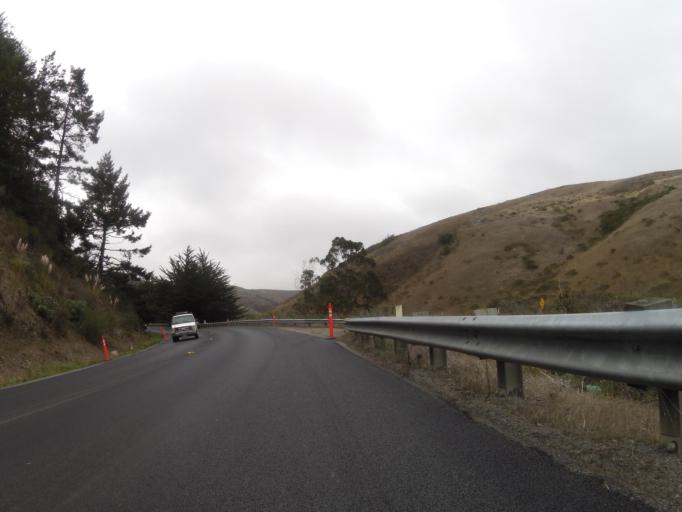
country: US
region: California
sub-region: Sonoma County
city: Bodega Bay
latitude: 38.3200
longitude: -123.0135
